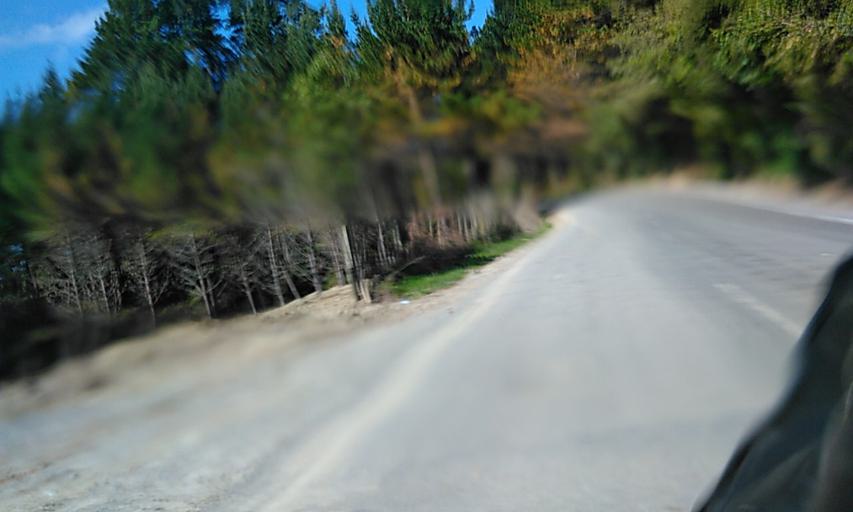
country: NZ
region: Gisborne
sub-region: Gisborne District
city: Gisborne
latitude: -38.3008
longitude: 178.1097
